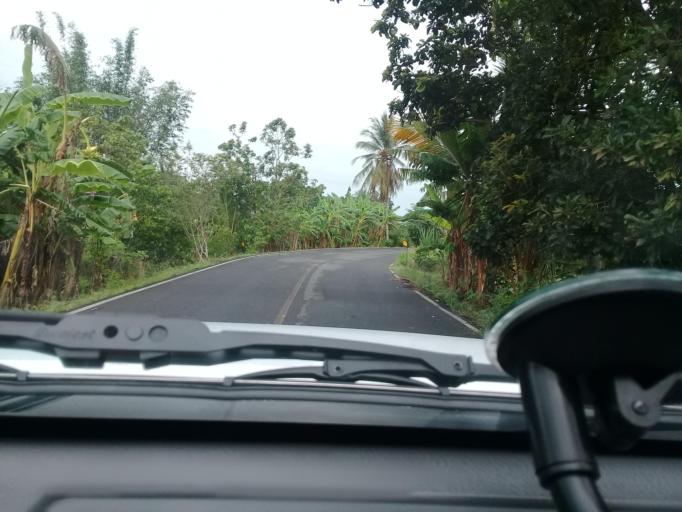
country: MX
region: Veracruz
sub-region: Paso de Ovejas
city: El Hatito
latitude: 19.3203
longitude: -96.3894
